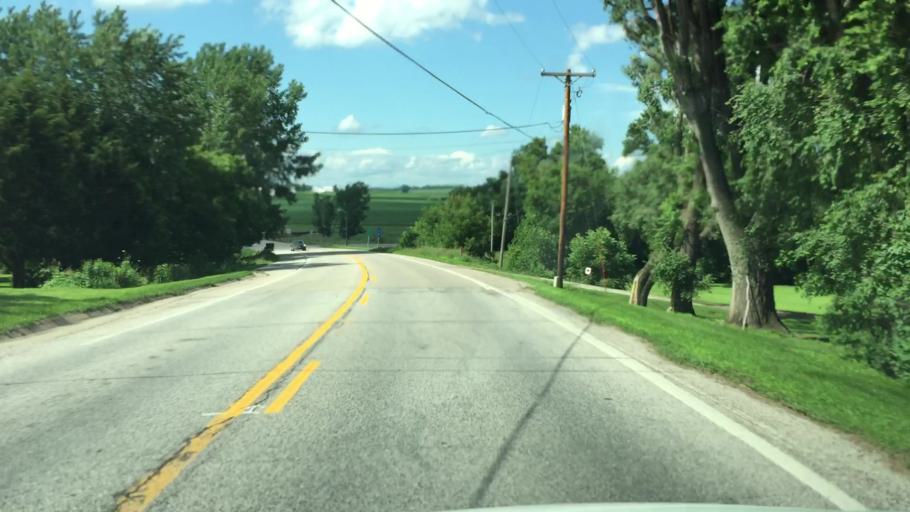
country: US
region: Iowa
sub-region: Johnson County
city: Solon
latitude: 41.8099
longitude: -91.4930
